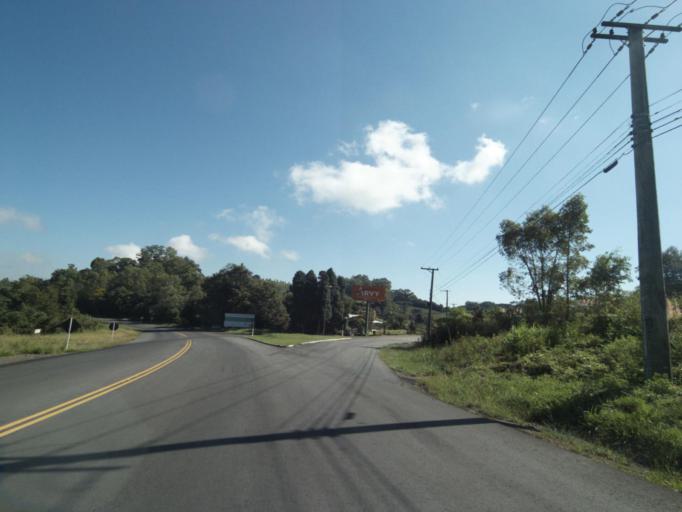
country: BR
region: Rio Grande do Sul
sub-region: Bento Goncalves
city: Bento Goncalves
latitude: -29.1181
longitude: -51.5419
